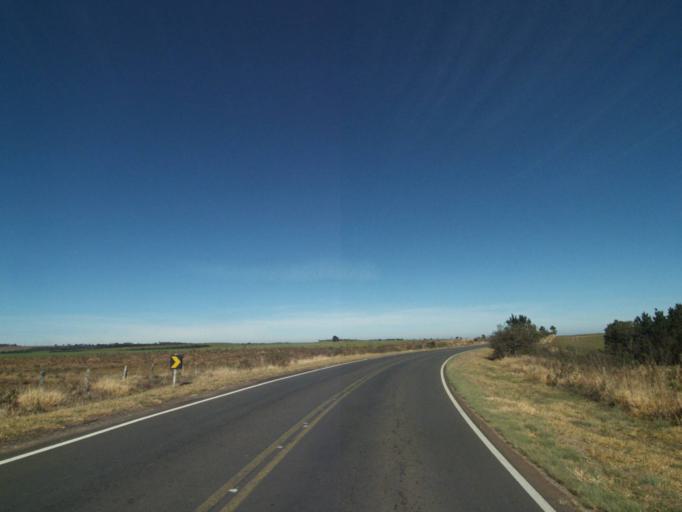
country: BR
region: Parana
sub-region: Tibagi
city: Tibagi
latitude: -24.6388
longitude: -50.2312
